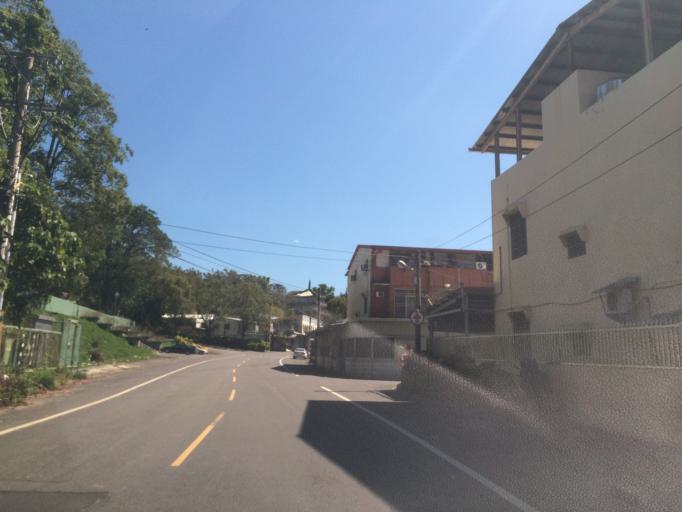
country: TW
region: Taiwan
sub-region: Yunlin
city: Douliu
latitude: 23.7097
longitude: 120.6053
